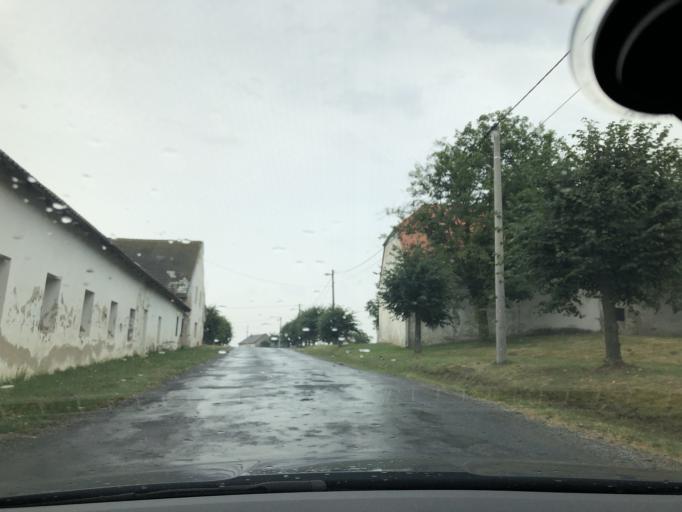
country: CZ
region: South Moravian
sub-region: Okres Znojmo
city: Jevisovice
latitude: 49.0287
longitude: 15.9783
